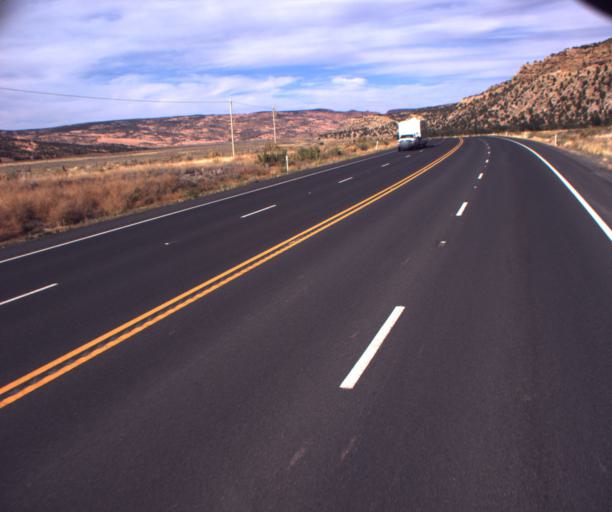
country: US
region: Arizona
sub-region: Navajo County
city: Kayenta
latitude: 36.5798
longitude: -110.4726
